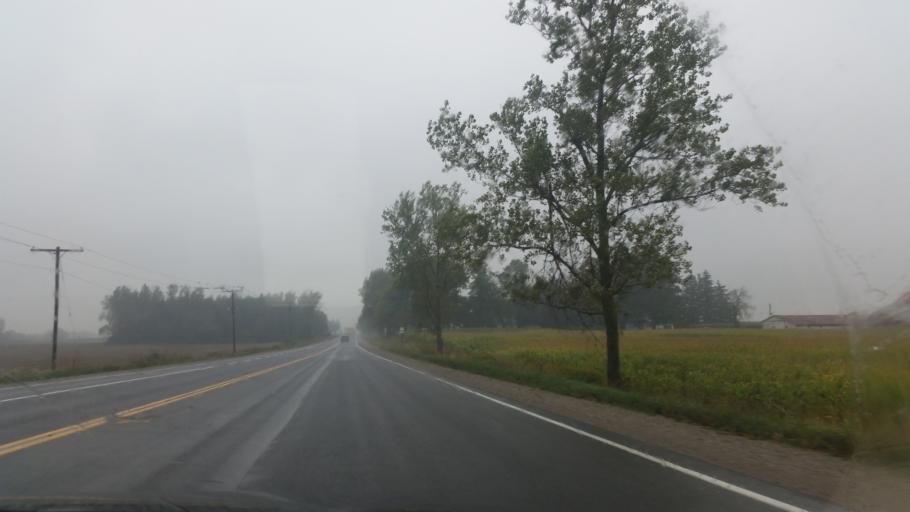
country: CA
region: Ontario
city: London
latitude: 43.2217
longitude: -81.1641
